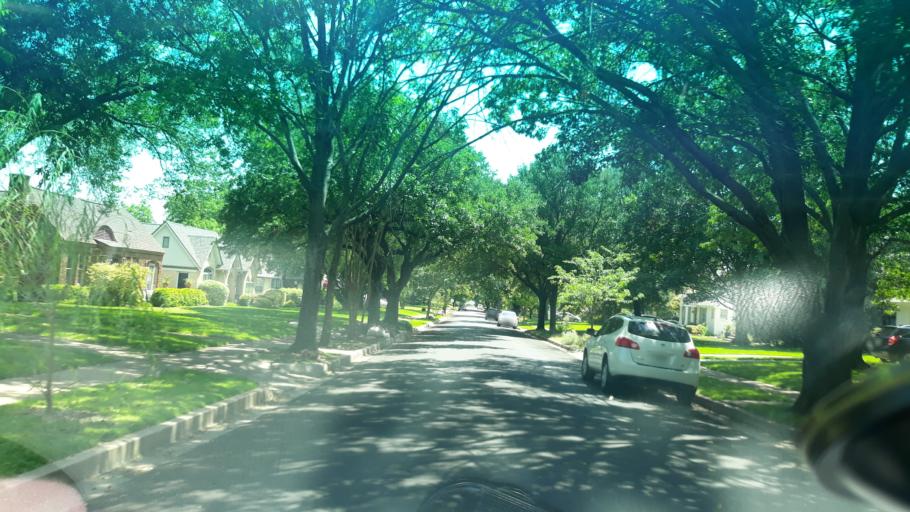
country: US
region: Texas
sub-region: Dallas County
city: Highland Park
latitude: 32.8141
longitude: -96.7397
